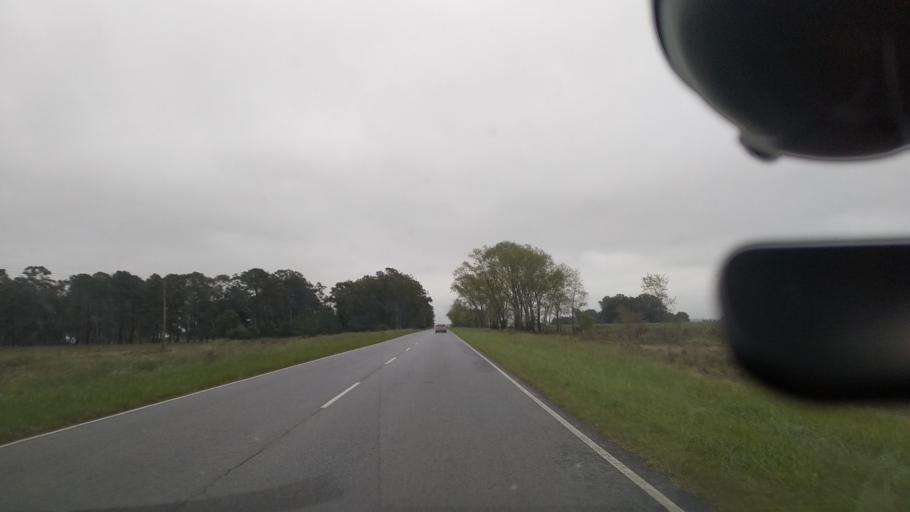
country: AR
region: Buenos Aires
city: Veronica
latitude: -35.3521
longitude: -57.4214
